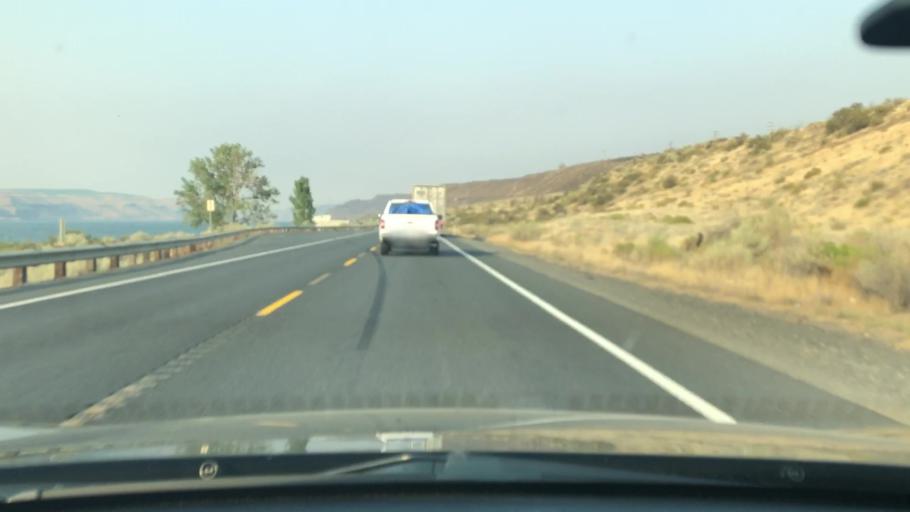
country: US
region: Oregon
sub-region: Umatilla County
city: Stanfield
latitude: 45.9284
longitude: -119.1015
